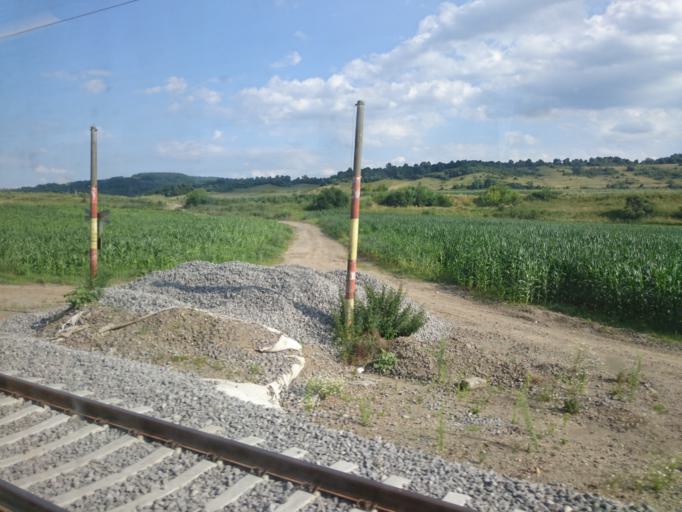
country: RO
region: Sibiu
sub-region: Comuna Laslea
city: Laslea
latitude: 46.2207
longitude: 24.6519
